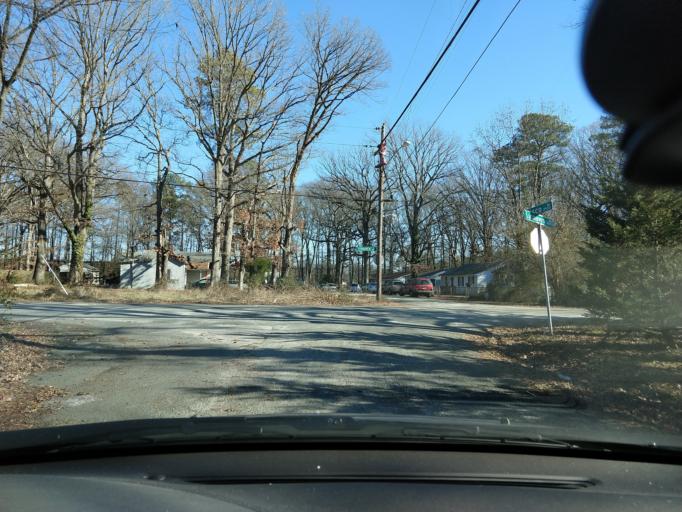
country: US
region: Virginia
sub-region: Chesterfield County
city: Bensley
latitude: 37.4688
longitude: -77.4410
